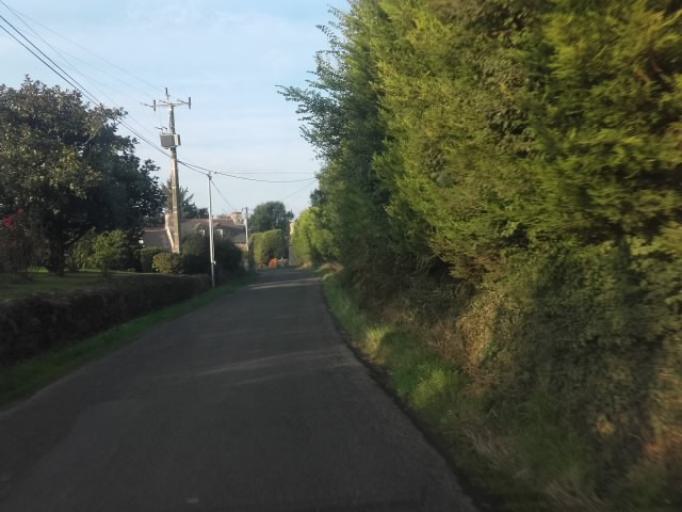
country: FR
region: Brittany
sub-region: Departement des Cotes-d'Armor
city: Pleguien
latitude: 48.6450
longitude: -2.9392
